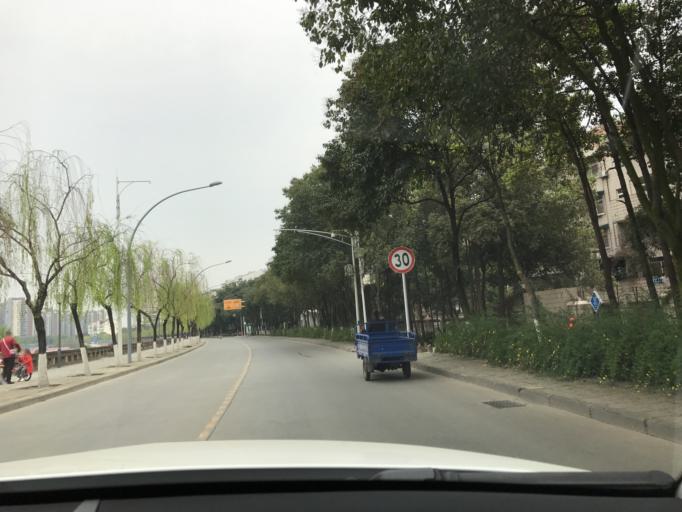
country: CN
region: Sichuan
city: Mianyang
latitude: 31.4579
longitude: 104.7048
